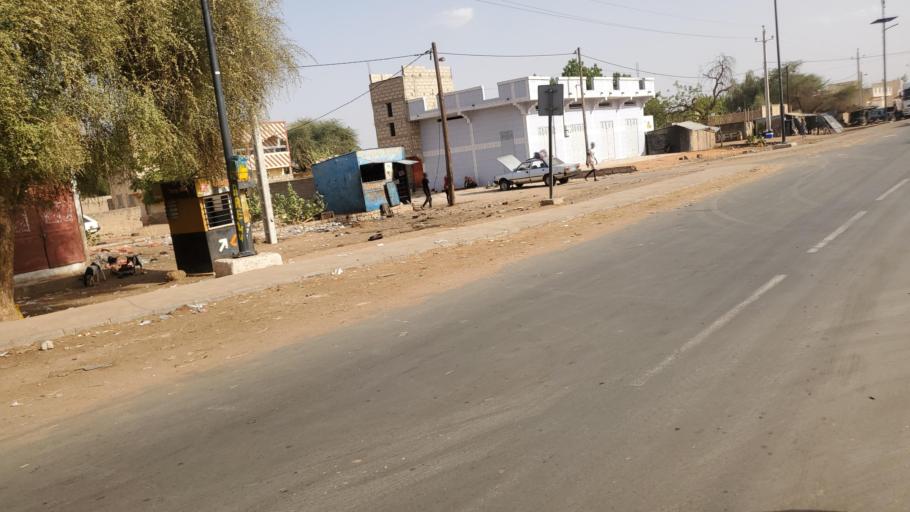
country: SN
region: Louga
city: Dara
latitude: 15.3485
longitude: -15.4892
